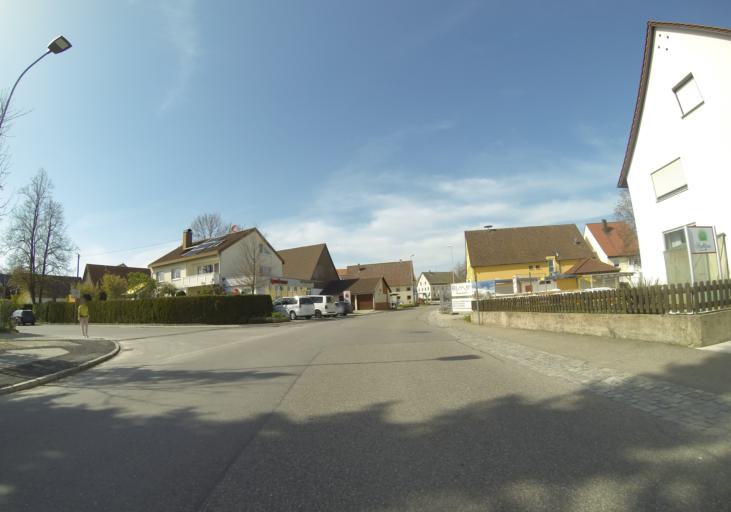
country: DE
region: Baden-Wuerttemberg
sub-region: Tuebingen Region
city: Huttisheim
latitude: 48.2787
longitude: 9.9433
